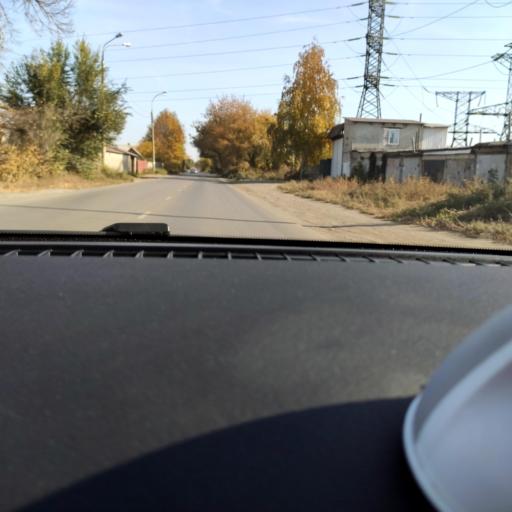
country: RU
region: Samara
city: Smyshlyayevka
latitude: 53.2333
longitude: 50.3165
